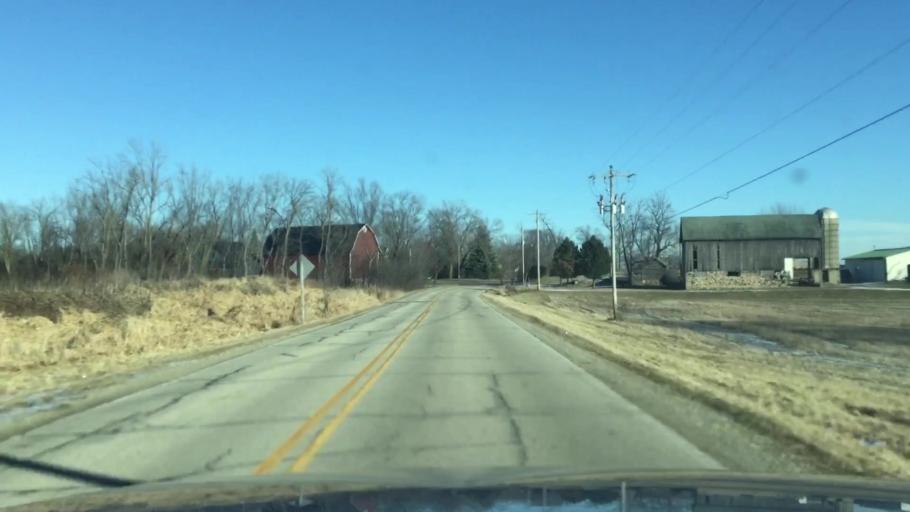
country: US
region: Wisconsin
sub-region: Racine County
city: Waterford
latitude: 42.7635
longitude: -88.1960
